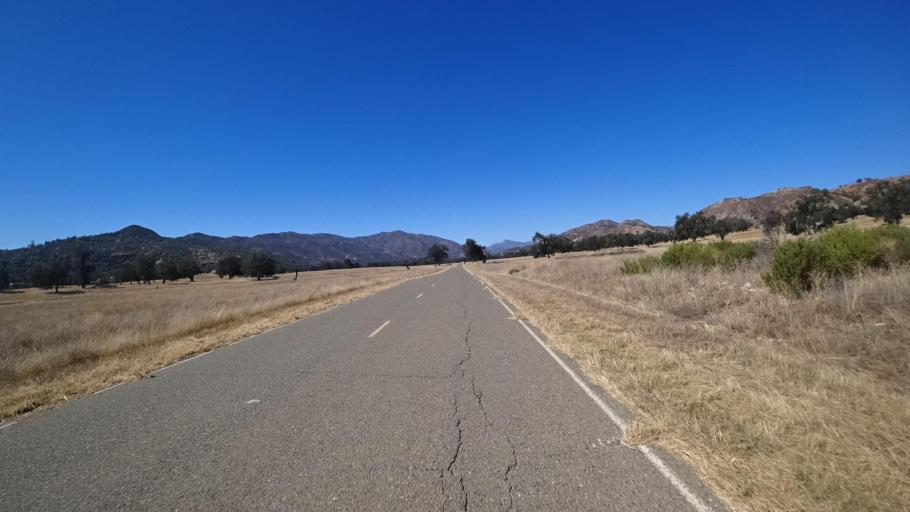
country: US
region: California
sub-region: Monterey County
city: King City
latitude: 35.9667
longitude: -121.3067
